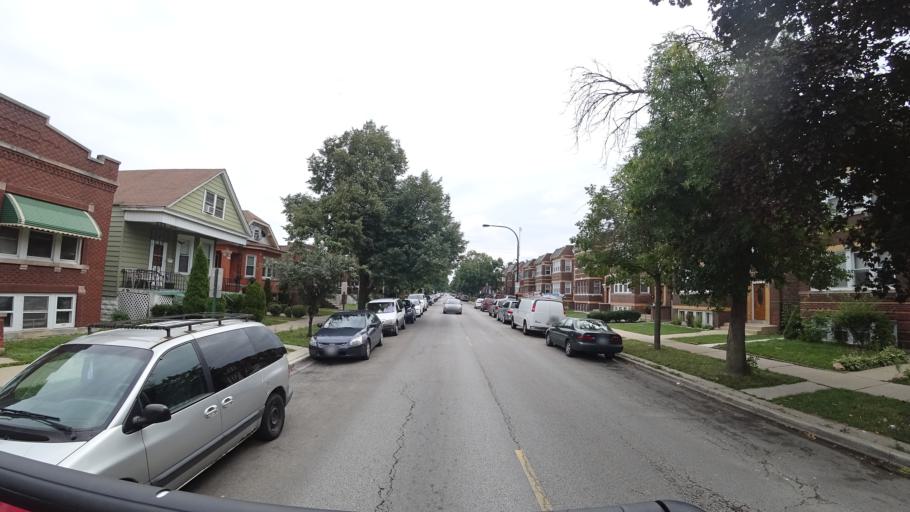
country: US
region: Illinois
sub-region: Cook County
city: Cicero
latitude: 41.8562
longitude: -87.7689
